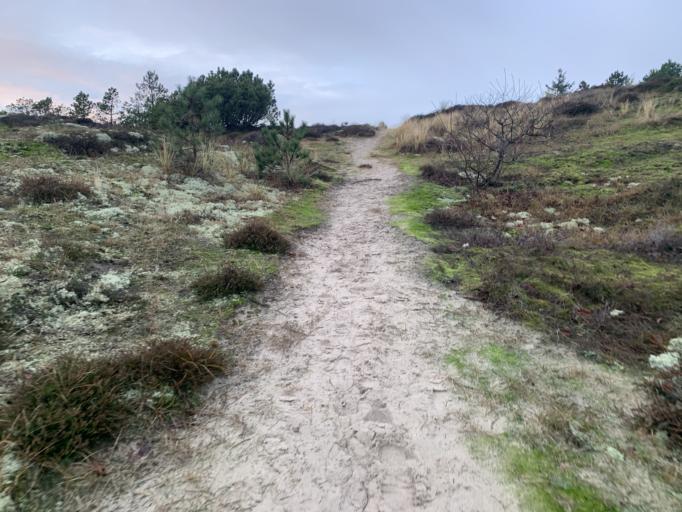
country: DE
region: Schleswig-Holstein
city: Nebel
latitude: 54.6405
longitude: 8.3459
